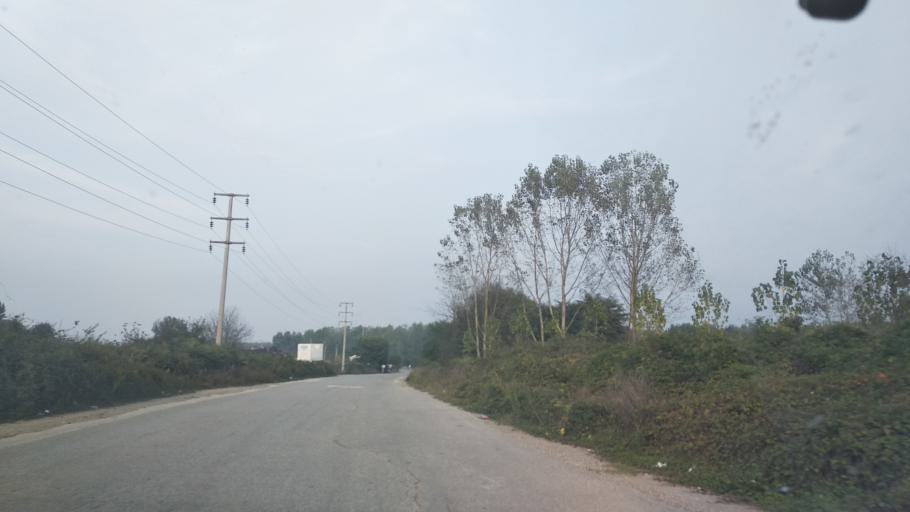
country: TR
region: Duzce
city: Duzce
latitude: 40.8047
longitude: 31.1765
